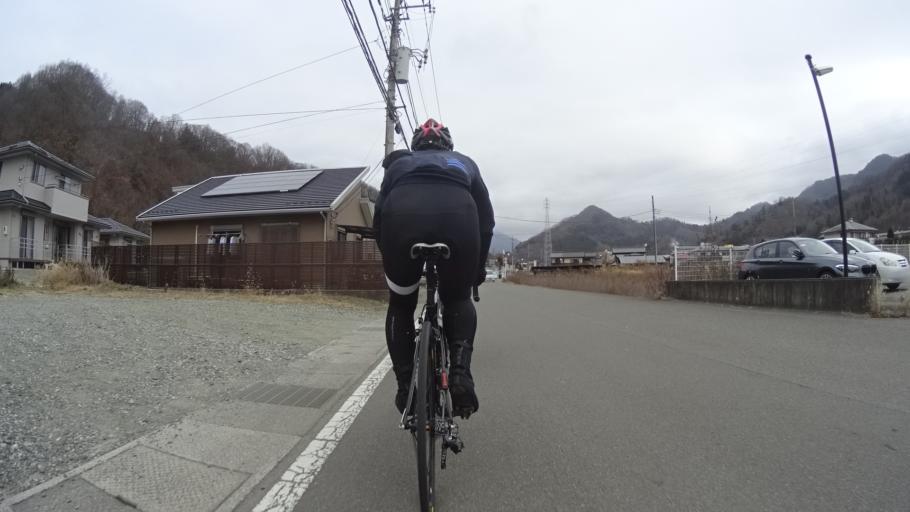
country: JP
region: Yamanashi
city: Otsuki
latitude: 35.5997
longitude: 138.9296
